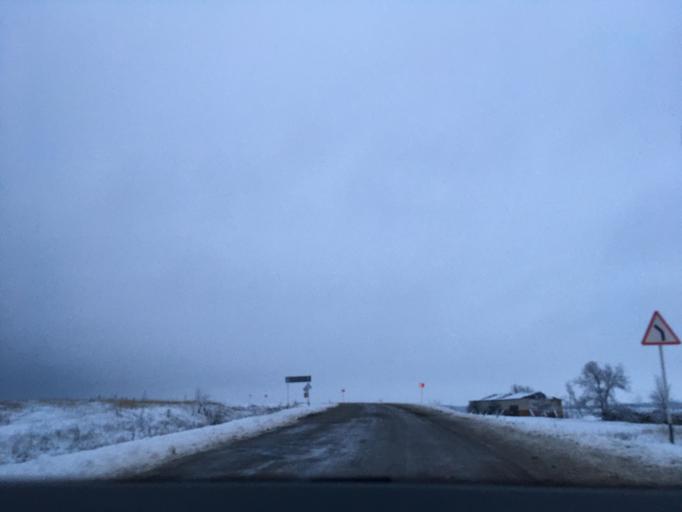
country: RU
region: Voronezj
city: Verkhniy Mamon
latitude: 50.0720
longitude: 40.3069
